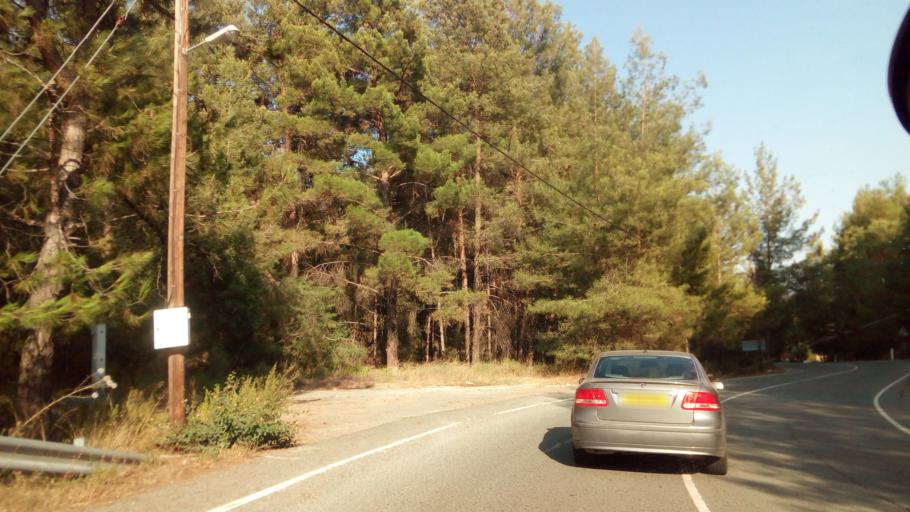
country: CY
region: Limassol
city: Pelendri
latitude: 34.8643
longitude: 32.8643
